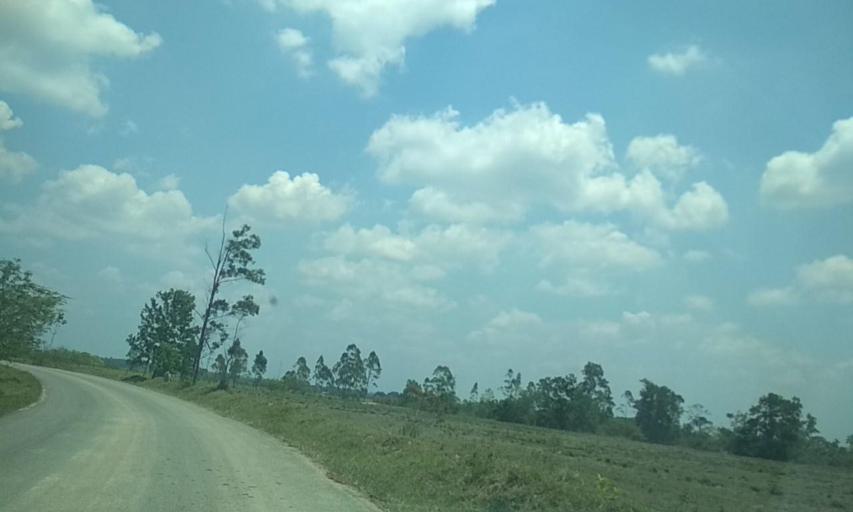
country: MX
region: Tabasco
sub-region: Huimanguillo
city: Francisco Rueda
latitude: 17.8086
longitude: -93.8675
